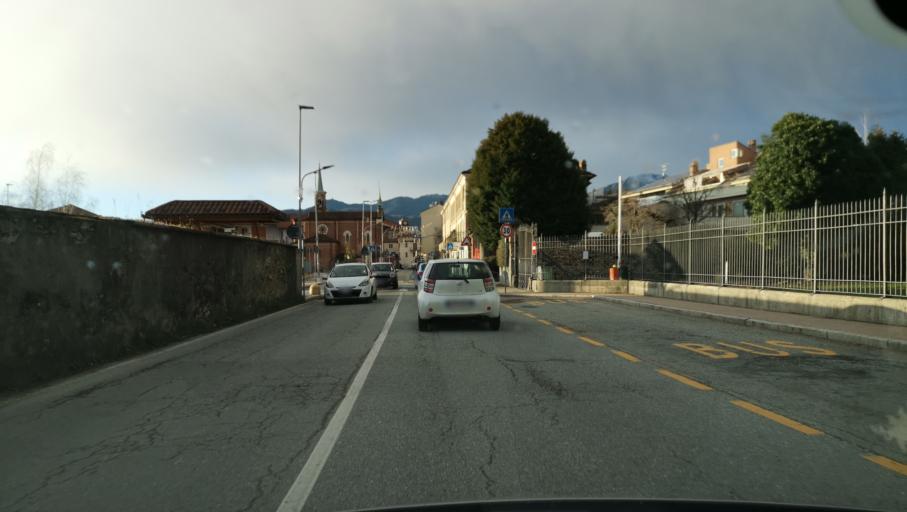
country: IT
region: Piedmont
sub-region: Provincia di Torino
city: Giaveno
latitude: 45.0464
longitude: 7.3544
